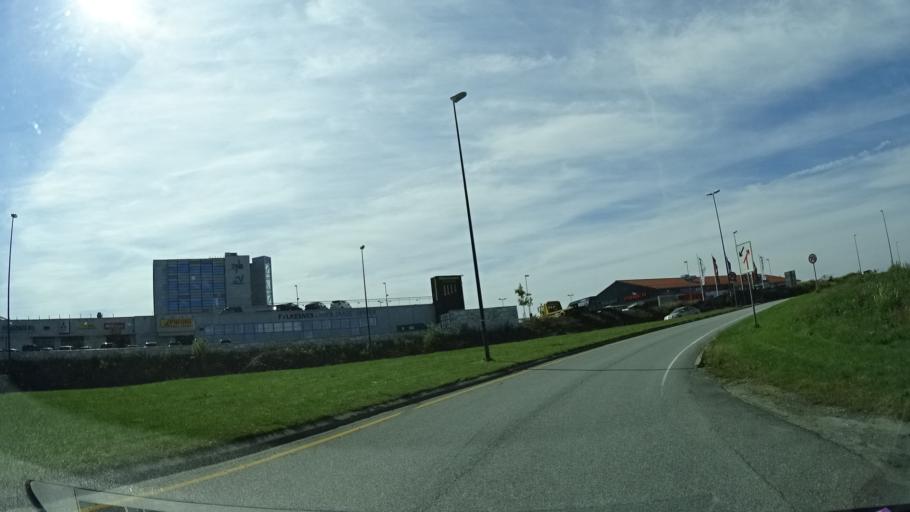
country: NO
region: Hordaland
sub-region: Stord
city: Leirvik
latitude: 59.7637
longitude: 5.4531
